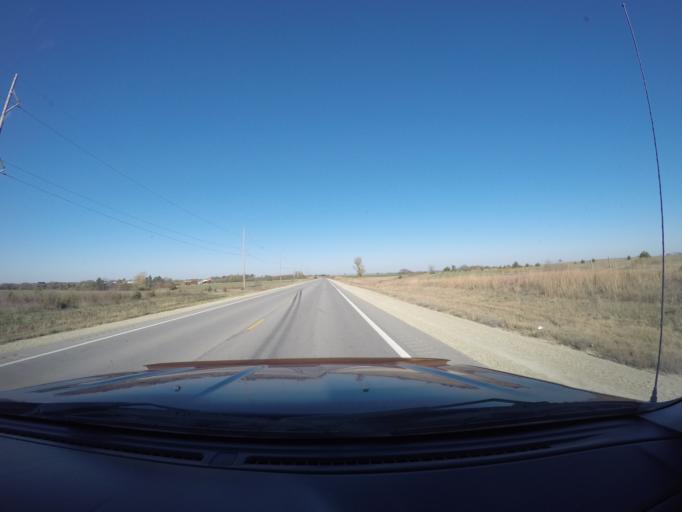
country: US
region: Kansas
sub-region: Riley County
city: Manhattan
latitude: 39.2667
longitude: -96.6853
